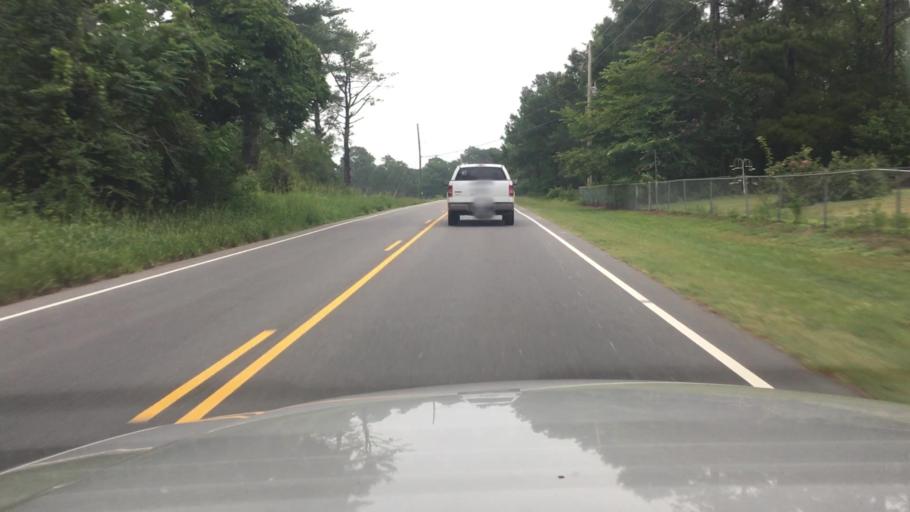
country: US
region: North Carolina
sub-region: Cumberland County
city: Hope Mills
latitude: 34.9749
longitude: -79.0023
